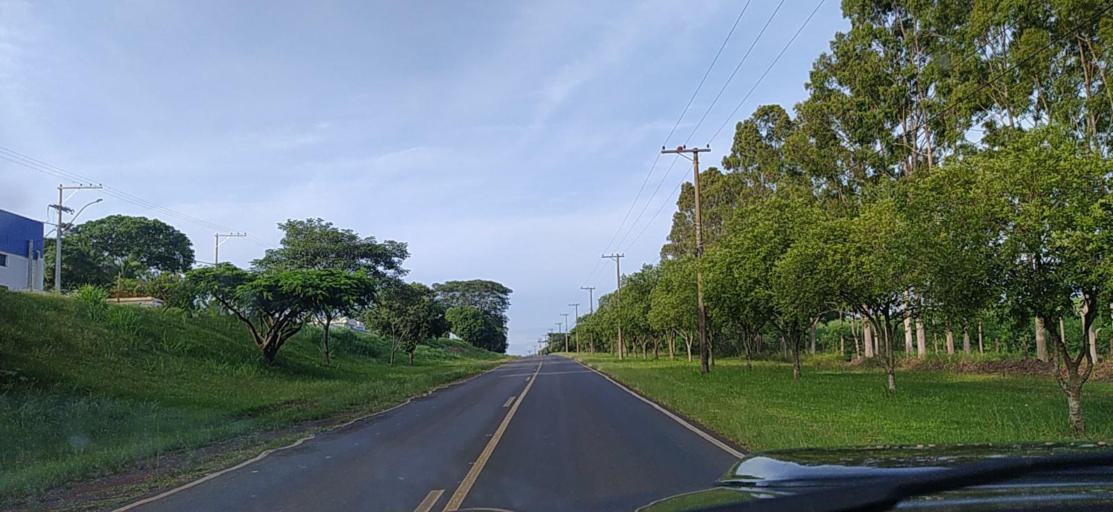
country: BR
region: Sao Paulo
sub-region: Pindorama
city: Pindorama
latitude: -21.1981
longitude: -48.9215
